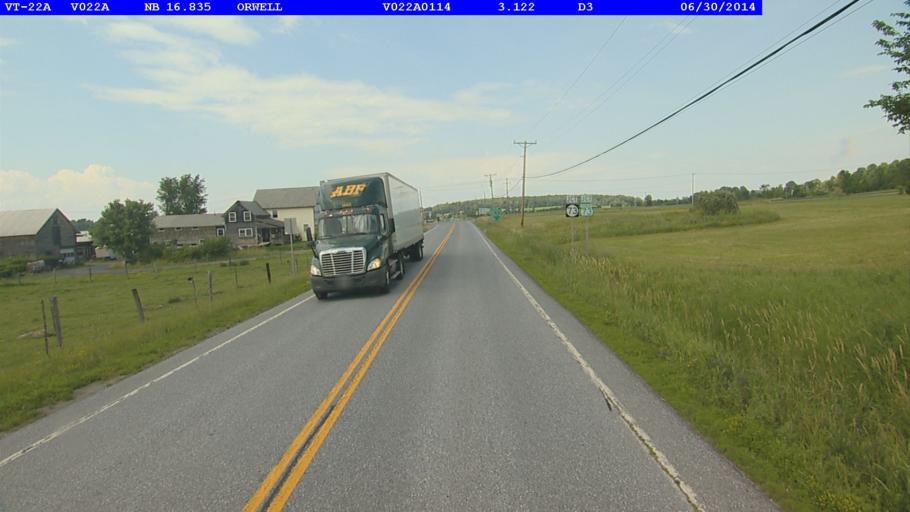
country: US
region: New York
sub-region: Essex County
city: Ticonderoga
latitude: 43.8020
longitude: -73.3053
